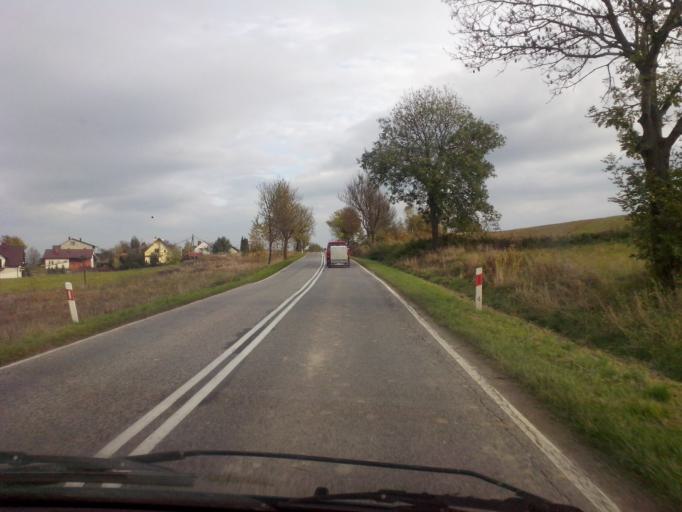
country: PL
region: Subcarpathian Voivodeship
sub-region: Powiat strzyzowski
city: Wisniowa
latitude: 49.8741
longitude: 21.6543
